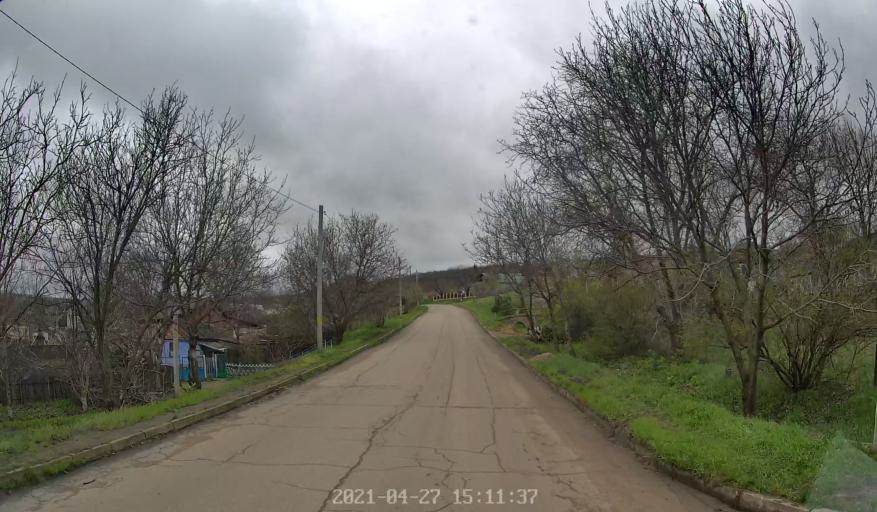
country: MD
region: Chisinau
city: Vadul lui Voda
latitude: 47.0307
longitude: 29.0259
